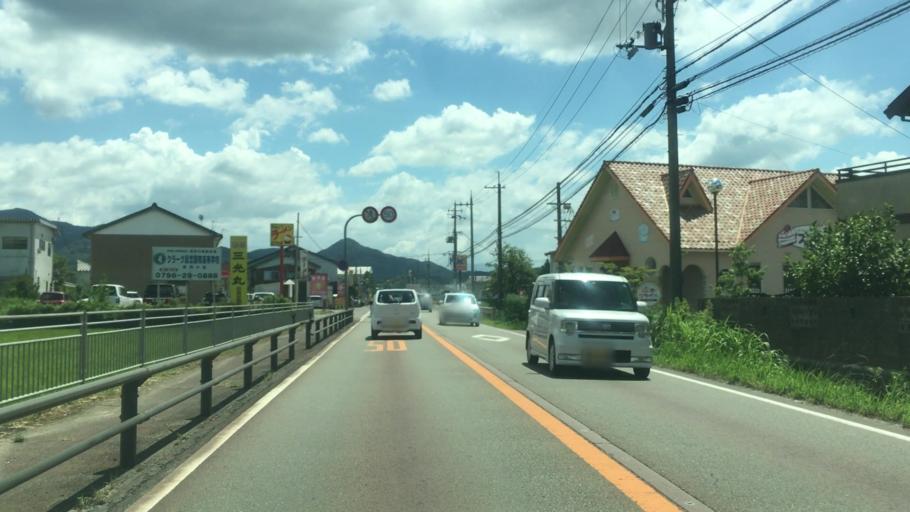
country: JP
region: Hyogo
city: Toyooka
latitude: 35.4950
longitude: 134.8014
